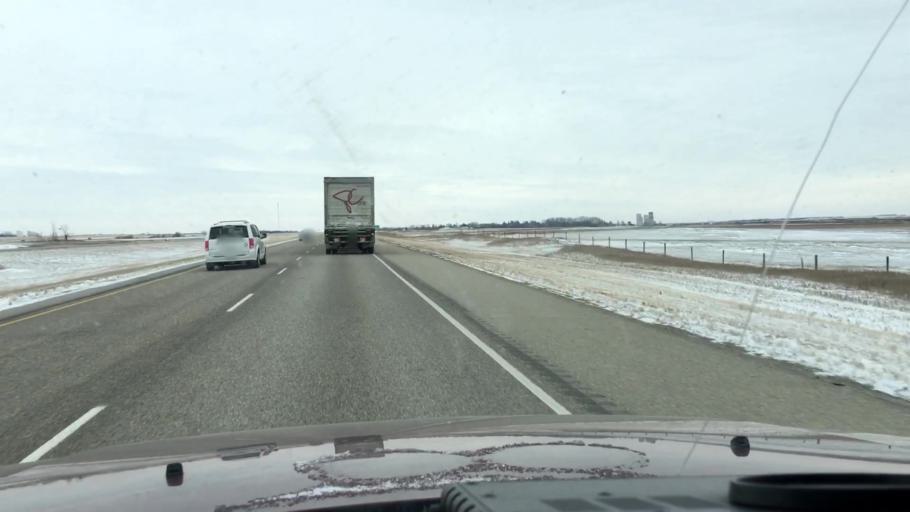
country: CA
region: Saskatchewan
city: Saskatoon
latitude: 51.5196
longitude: -106.2928
